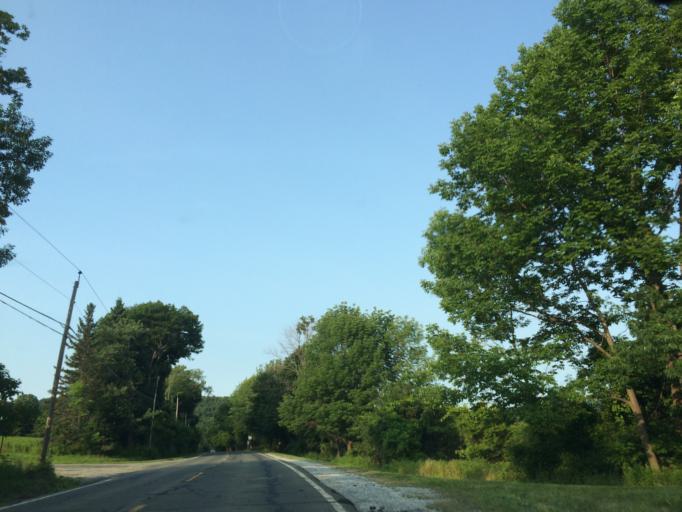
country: US
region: Massachusetts
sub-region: Berkshire County
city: Richmond
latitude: 42.3919
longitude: -73.3897
